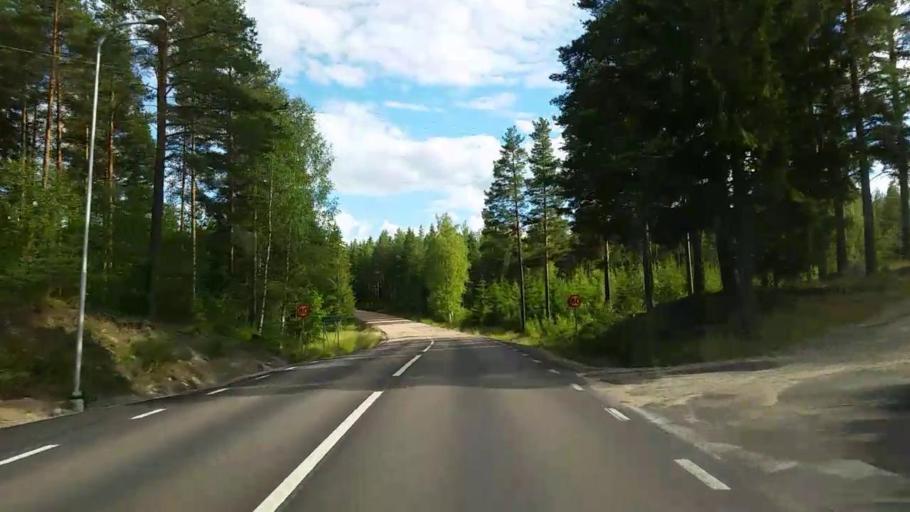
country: SE
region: Gaevleborg
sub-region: Ljusdals Kommun
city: Farila
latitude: 61.9254
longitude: 15.8735
